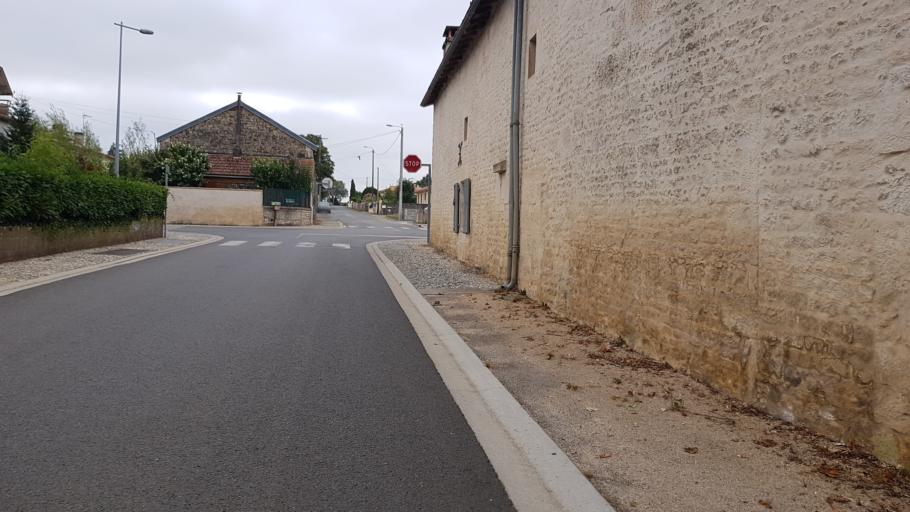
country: FR
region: Poitou-Charentes
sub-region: Departement des Deux-Sevres
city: Vouille
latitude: 46.3240
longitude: -0.3255
